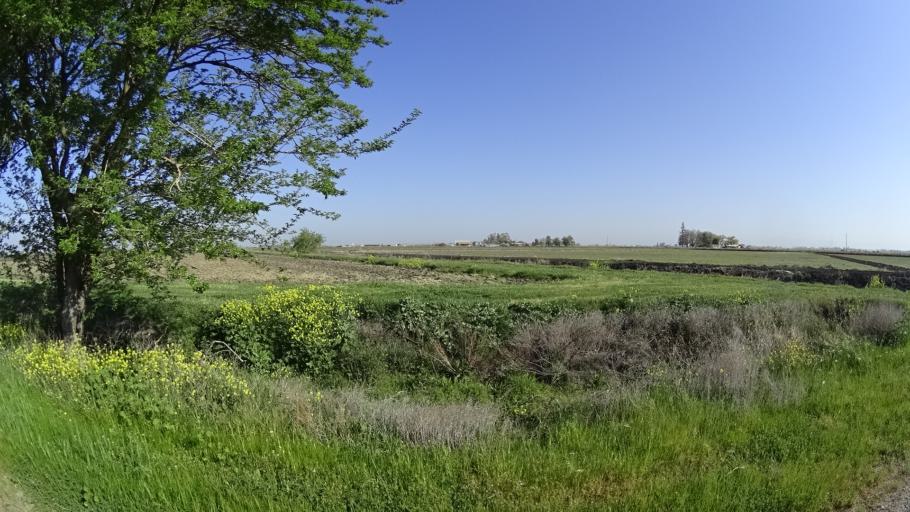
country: US
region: California
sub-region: Glenn County
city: Willows
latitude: 39.5654
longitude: -122.0674
